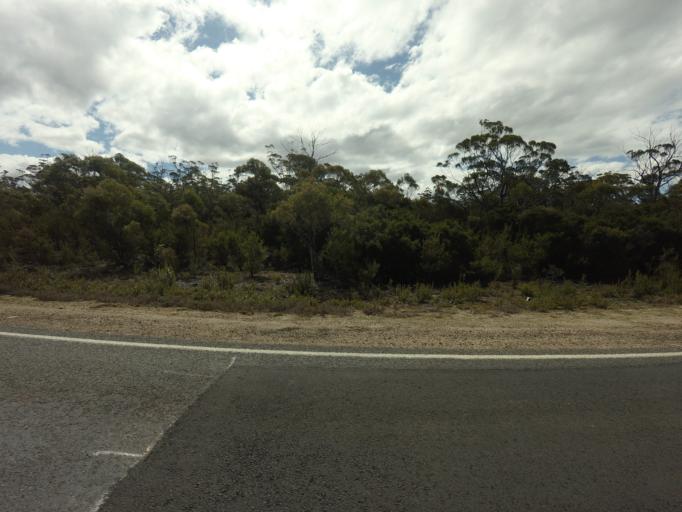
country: AU
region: Tasmania
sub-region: Break O'Day
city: St Helens
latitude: -42.0160
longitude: 147.9575
